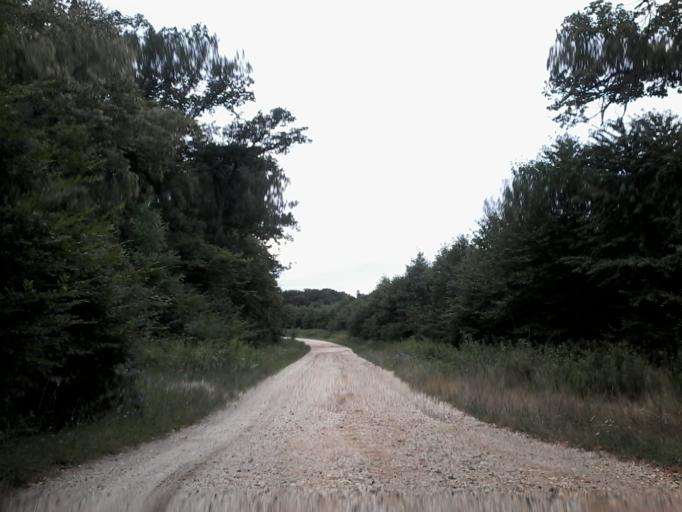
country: HU
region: Vas
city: Sarvar
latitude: 47.1585
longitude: 17.0209
